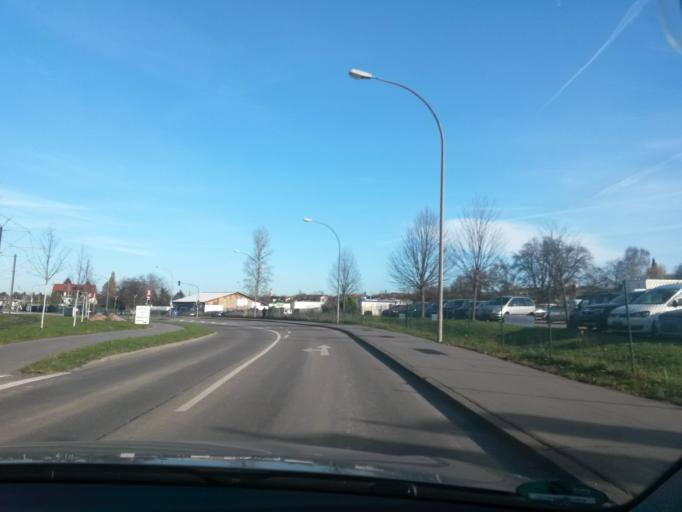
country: DE
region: Baden-Wuerttemberg
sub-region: Freiburg Region
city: Gundelfingen
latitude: 48.0307
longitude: 7.8627
